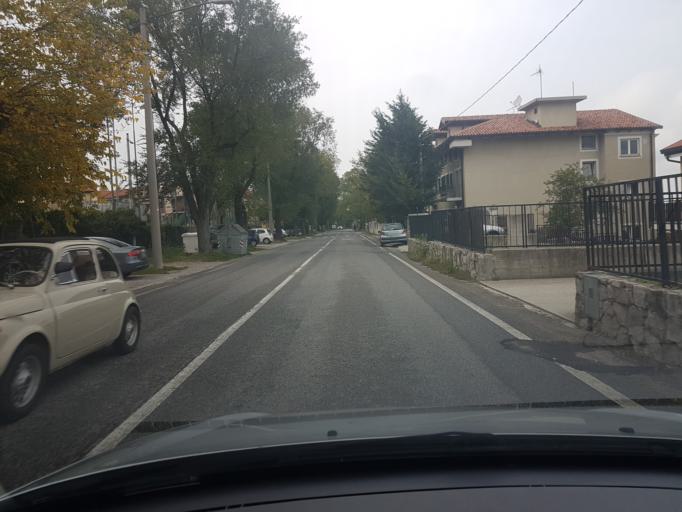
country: IT
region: Friuli Venezia Giulia
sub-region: Provincia di Trieste
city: Santa Croce
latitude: 45.7362
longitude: 13.6931
